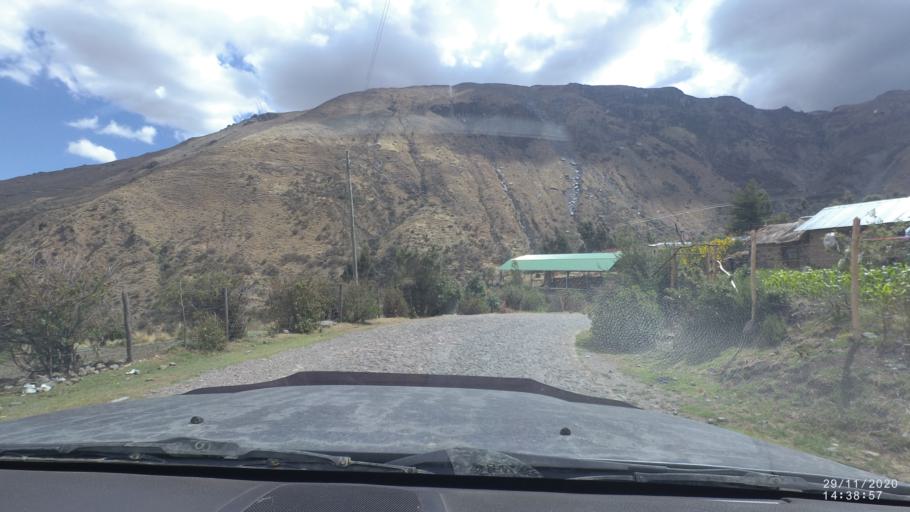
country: BO
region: Cochabamba
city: Sipe Sipe
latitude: -17.2731
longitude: -66.3290
